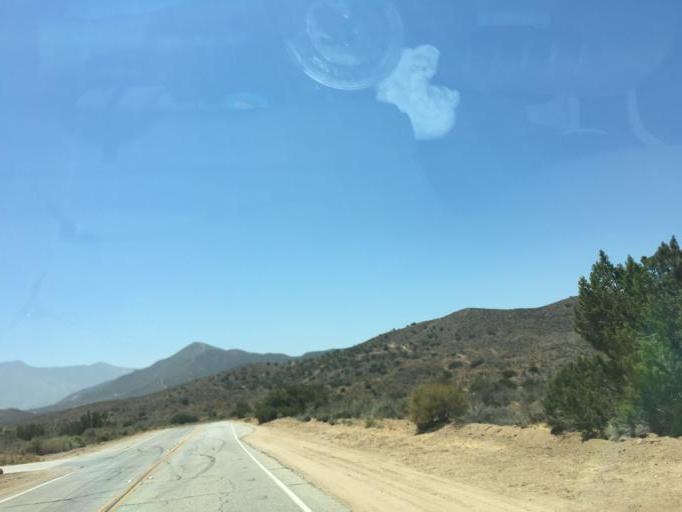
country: US
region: California
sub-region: Los Angeles County
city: Acton
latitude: 34.4949
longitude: -118.2189
